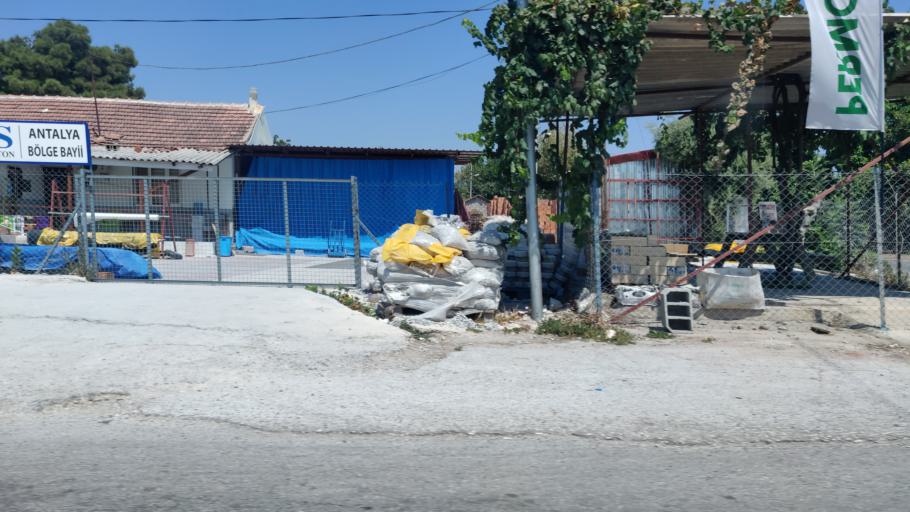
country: TR
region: Antalya
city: Antalya
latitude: 36.9002
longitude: 30.6347
